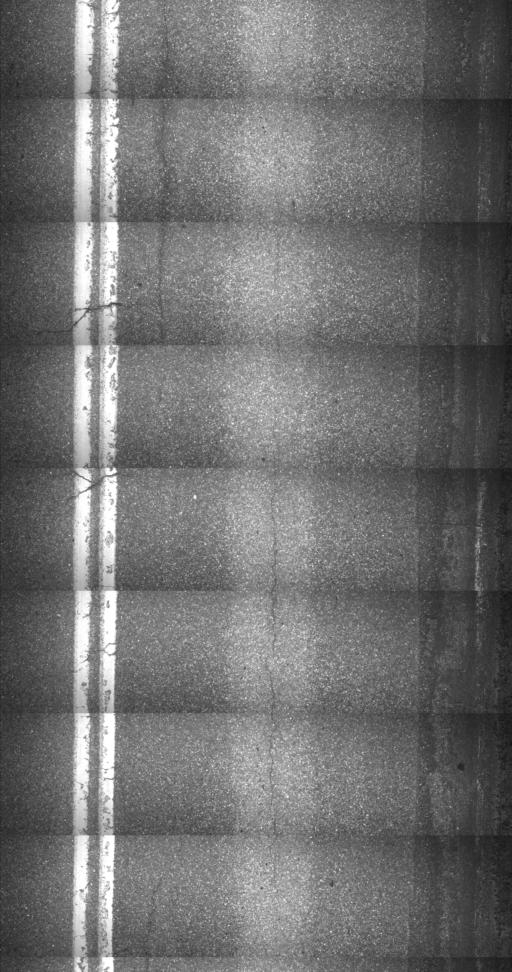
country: US
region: Vermont
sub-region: Windsor County
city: Windsor
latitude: 43.5313
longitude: -72.4044
